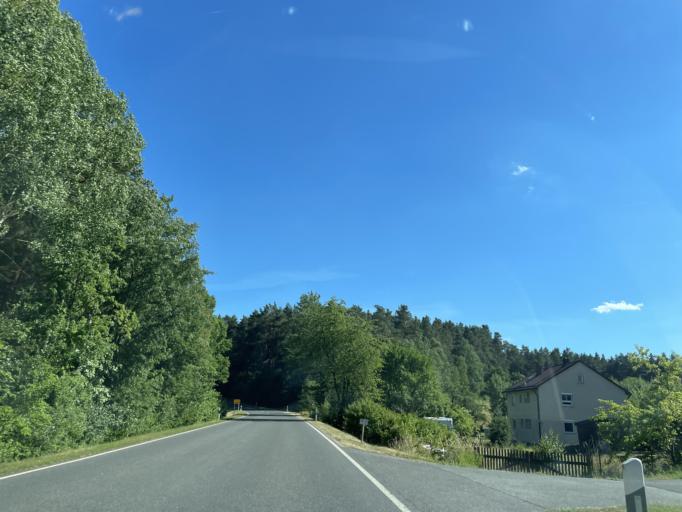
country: DE
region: Bavaria
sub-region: Upper Palatinate
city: Trabitz
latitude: 49.7949
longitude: 11.9030
